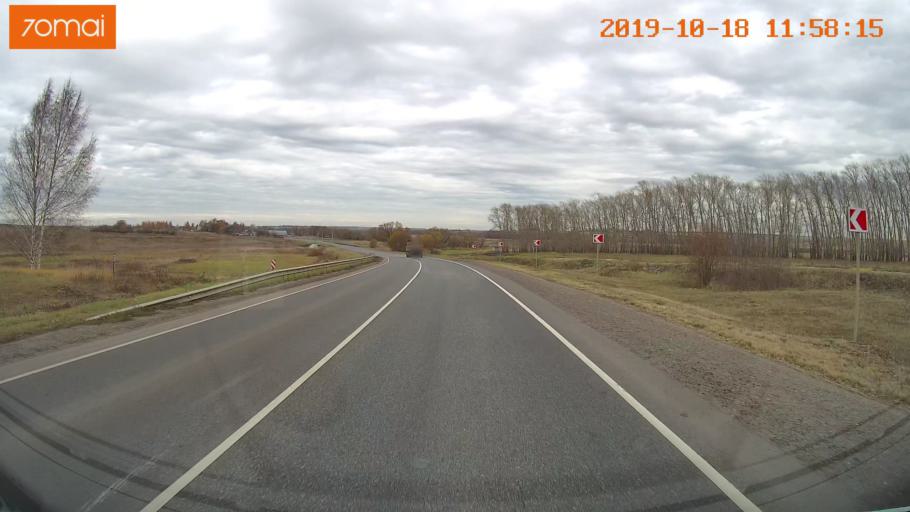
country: RU
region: Rjazan
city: Mikhaylov
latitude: 54.2697
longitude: 39.1646
